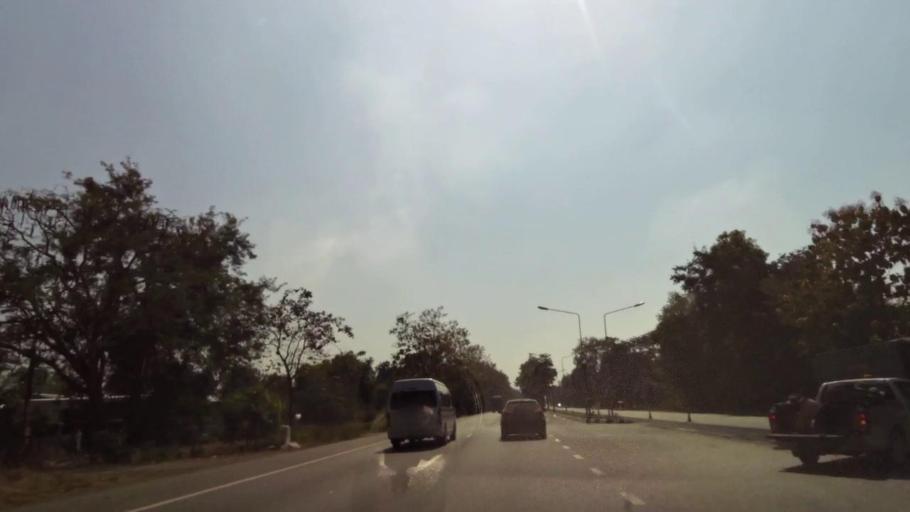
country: TH
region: Phichit
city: Bueng Na Rang
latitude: 16.0634
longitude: 100.1232
